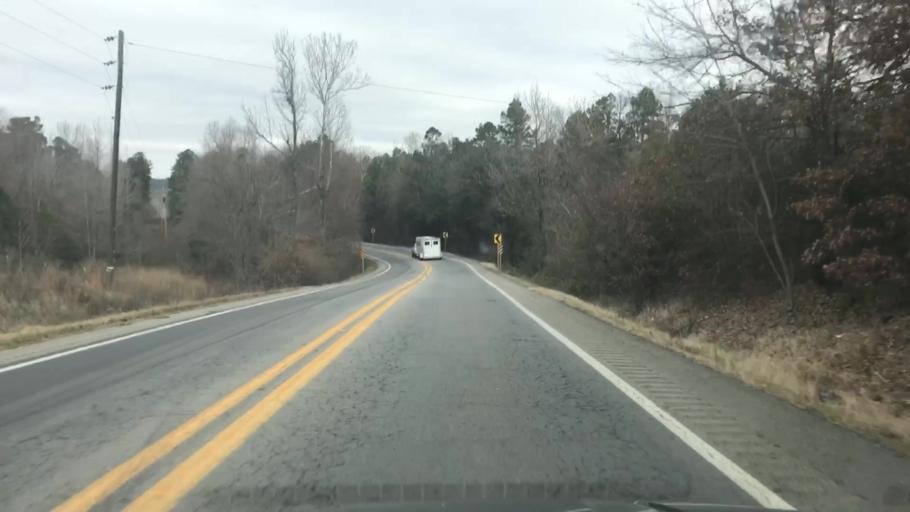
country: US
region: Arkansas
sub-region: Scott County
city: Waldron
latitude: 34.9505
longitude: -94.1052
